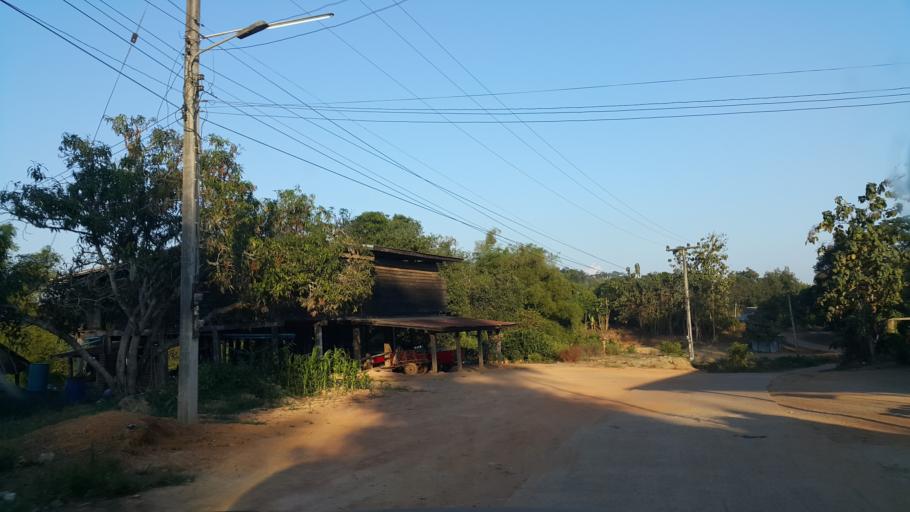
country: TH
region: Sukhothai
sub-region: Amphoe Si Satchanalai
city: Si Satchanalai
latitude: 17.6202
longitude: 99.6244
